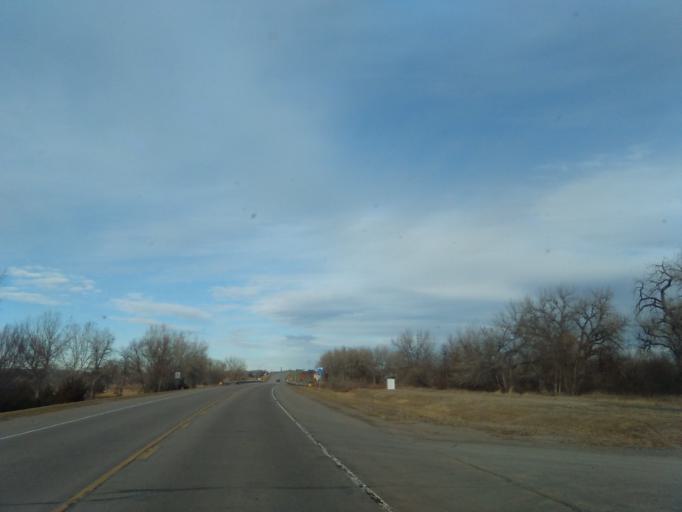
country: US
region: Nebraska
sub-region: Morrill County
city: Bridgeport
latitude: 41.6756
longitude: -103.0980
